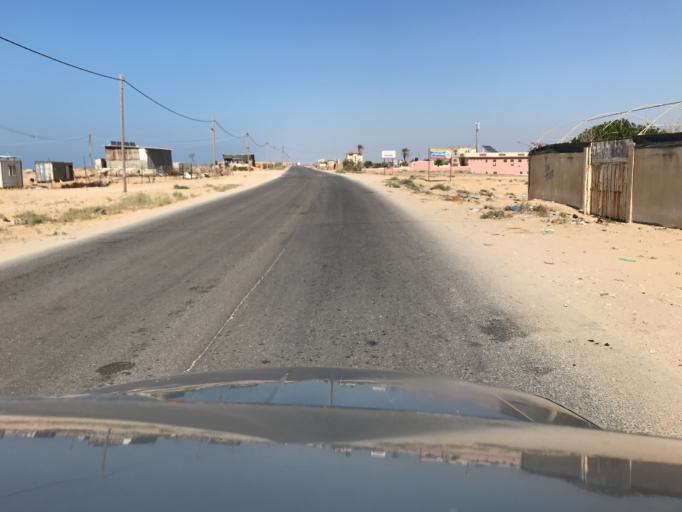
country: PS
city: Wadi as Salqa
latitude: 31.3961
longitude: 34.3045
